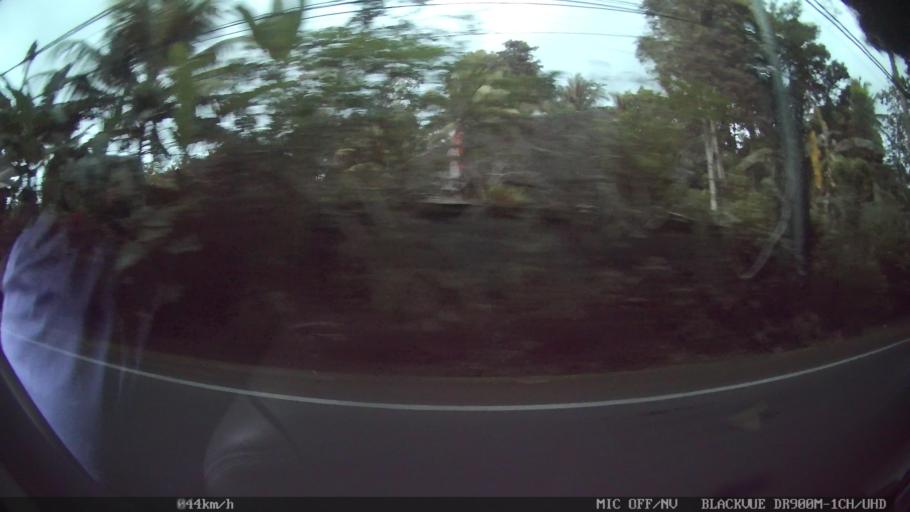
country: ID
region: Bali
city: Bunutan
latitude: -8.4574
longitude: 115.2451
